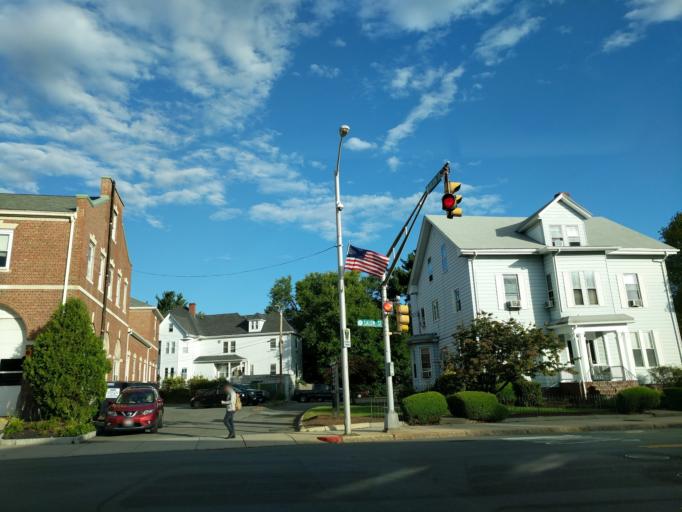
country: US
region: Massachusetts
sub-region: Middlesex County
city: Malden
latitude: 42.4279
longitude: -71.0640
